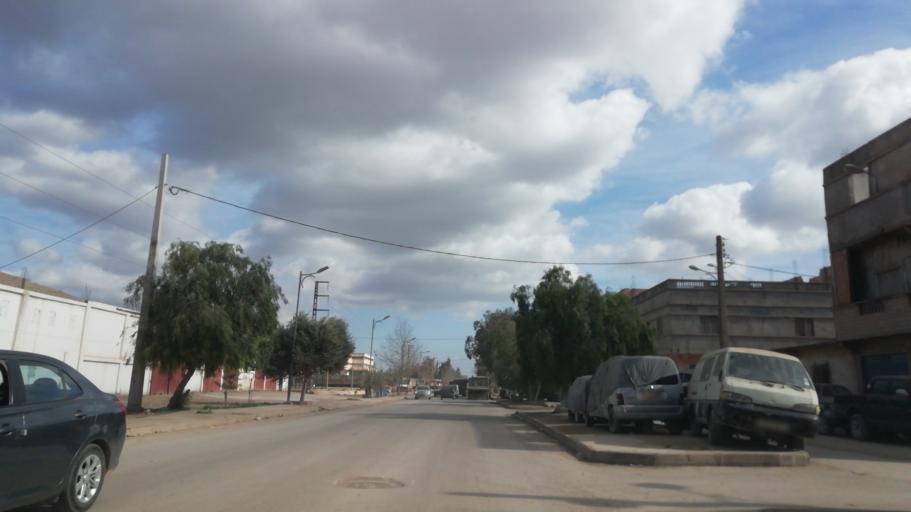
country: DZ
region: Oran
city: Es Senia
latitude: 35.6518
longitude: -0.5763
